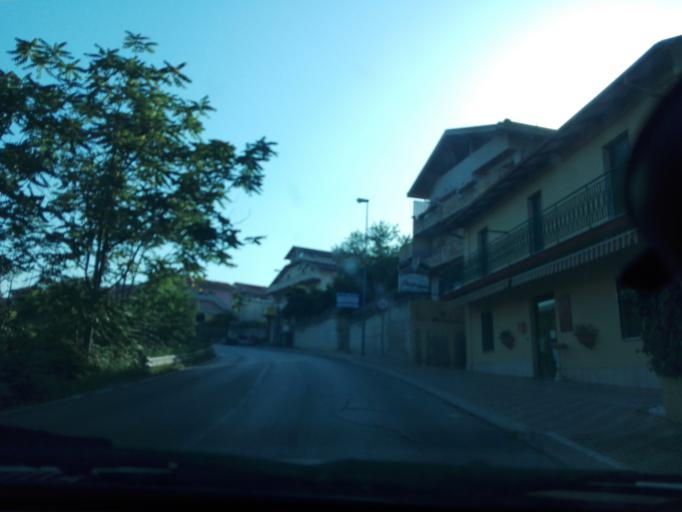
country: IT
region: Abruzzo
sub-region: Provincia di Pescara
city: Cappelle sul Tavo
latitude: 42.4704
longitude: 14.1070
